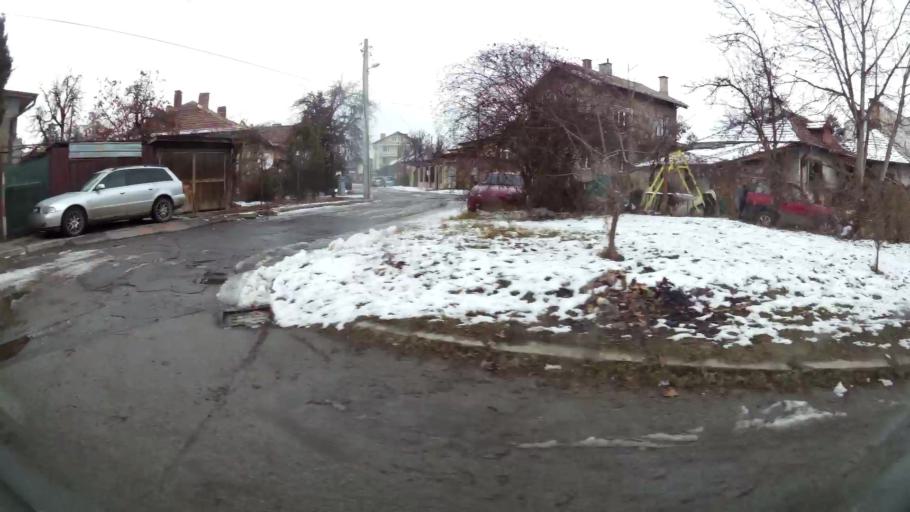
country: BG
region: Sofia-Capital
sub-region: Stolichna Obshtina
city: Sofia
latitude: 42.7257
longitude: 23.3421
